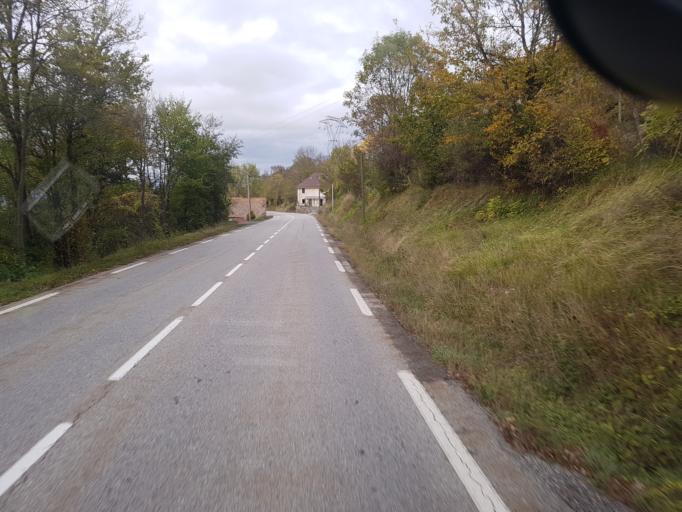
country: FR
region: Rhone-Alpes
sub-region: Departement de l'Isere
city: Le Gua
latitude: 44.9782
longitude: 5.6445
